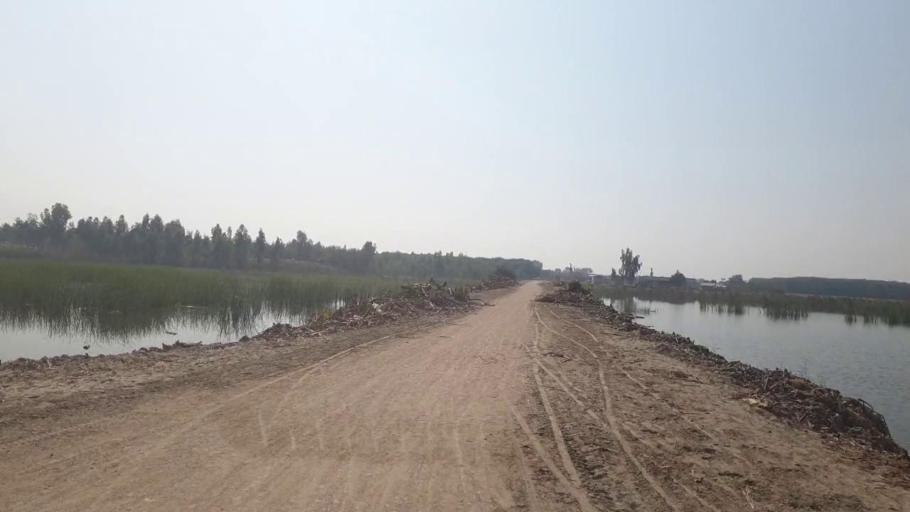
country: PK
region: Sindh
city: Tando Adam
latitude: 25.6283
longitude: 68.7253
